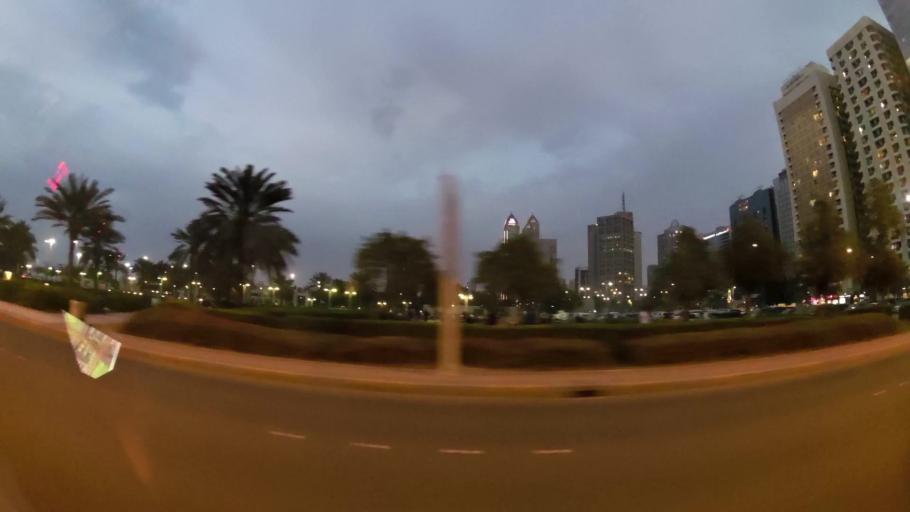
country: AE
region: Abu Dhabi
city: Abu Dhabi
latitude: 24.4940
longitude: 54.3597
